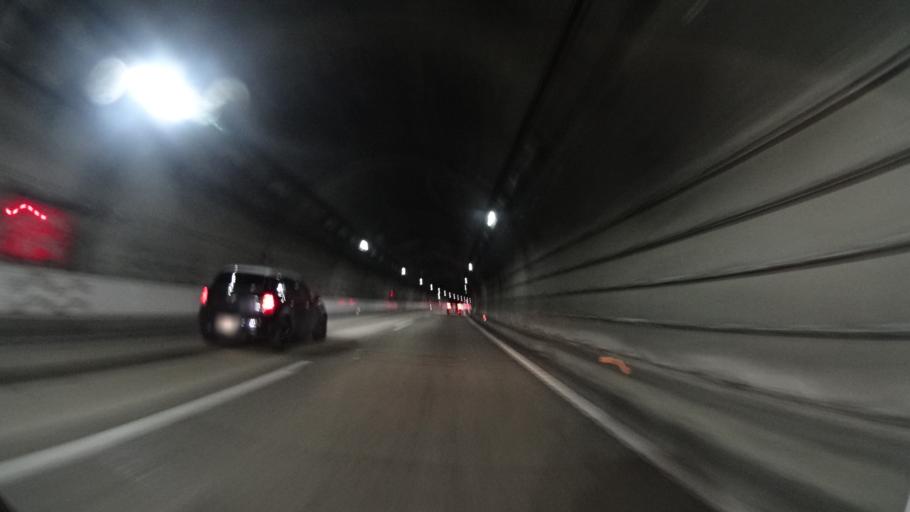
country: JP
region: Hyogo
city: Himeji
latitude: 34.8746
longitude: 134.6906
